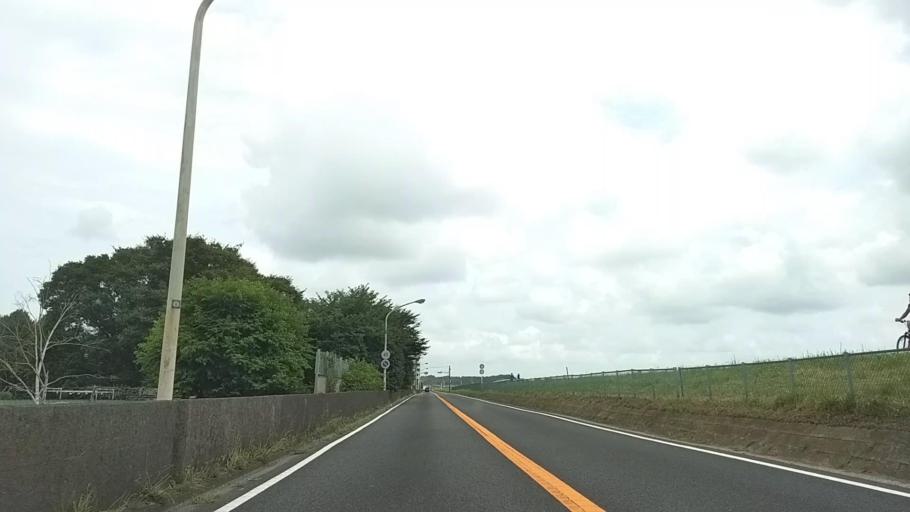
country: JP
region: Kanagawa
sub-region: Kawasaki-shi
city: Kawasaki
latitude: 35.5719
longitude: 139.6715
